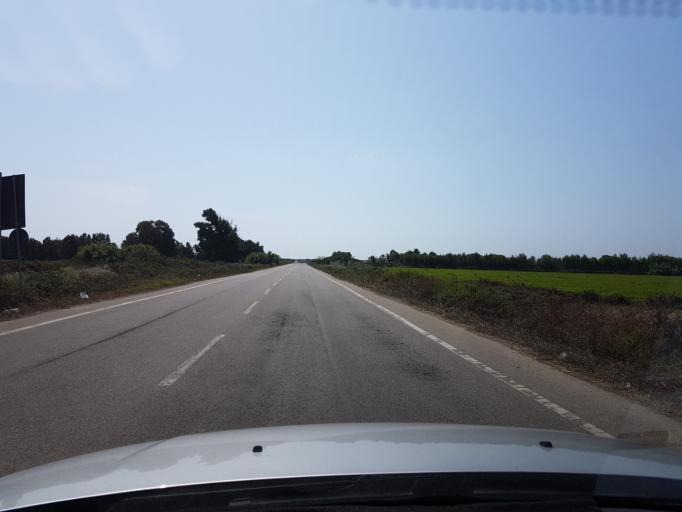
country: IT
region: Sardinia
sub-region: Provincia di Oristano
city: Cabras
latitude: 39.9190
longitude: 8.5352
